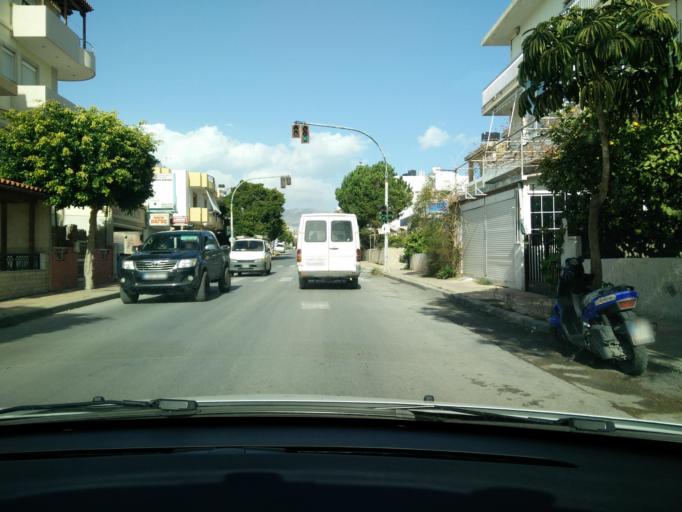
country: GR
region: Crete
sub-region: Nomos Lasithiou
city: Ierapetra
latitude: 35.0118
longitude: 25.7361
